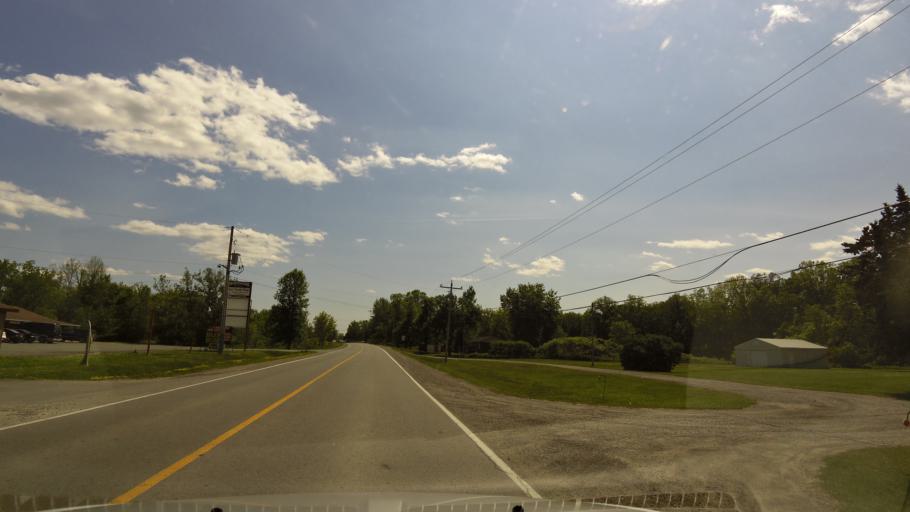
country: CA
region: Ontario
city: Ancaster
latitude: 43.0950
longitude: -80.1006
